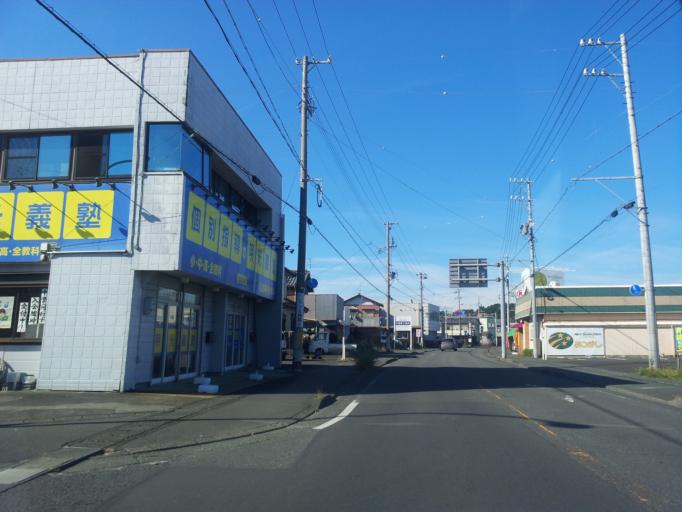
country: JP
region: Shizuoka
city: Sagara
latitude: 34.6834
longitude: 138.1939
